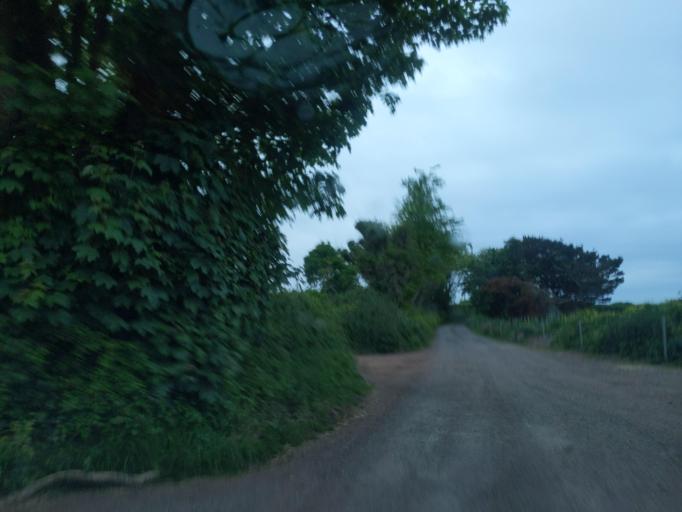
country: GB
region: England
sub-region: Borough of Torbay
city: Brixham
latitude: 50.3625
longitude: -3.5311
